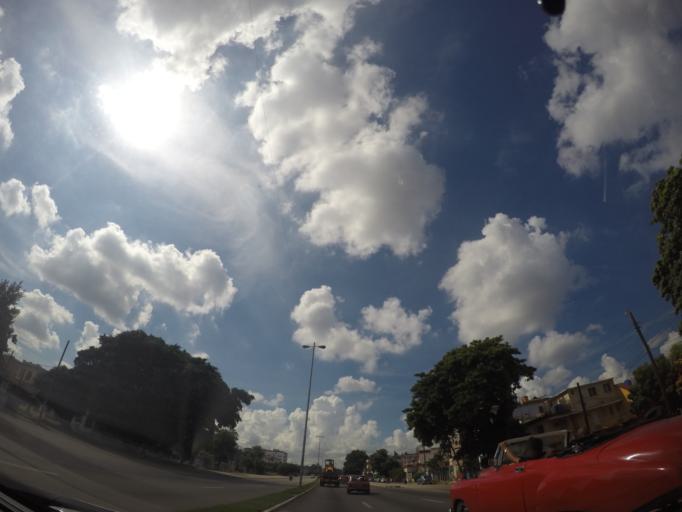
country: CU
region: La Habana
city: Havana
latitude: 23.1134
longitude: -82.4179
